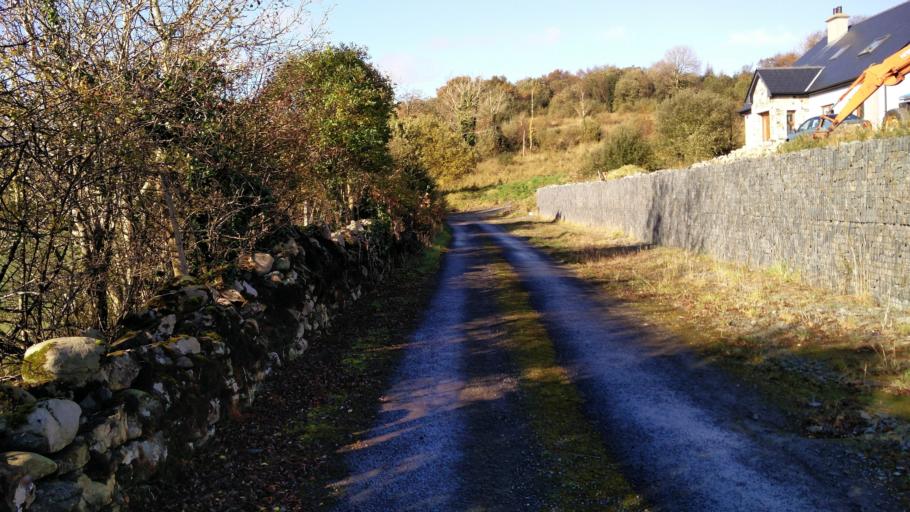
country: IE
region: Connaught
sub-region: Maigh Eo
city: Westport
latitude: 53.7805
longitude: -9.4511
